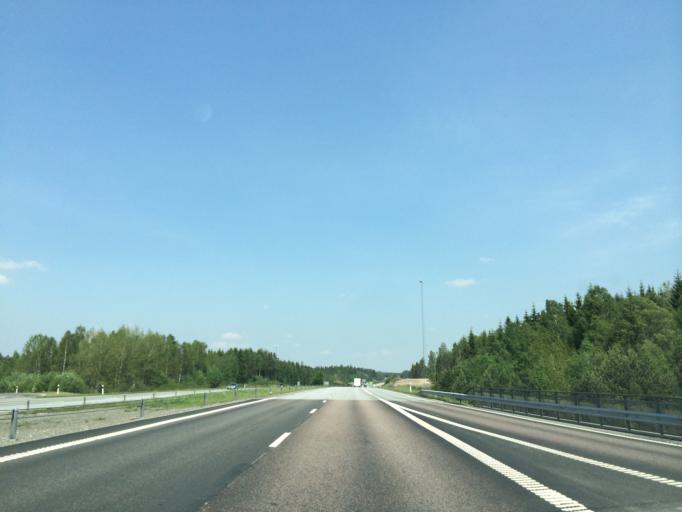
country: SE
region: Joenkoeping
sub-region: Varnamo Kommun
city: Varnamo
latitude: 57.1987
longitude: 14.0817
